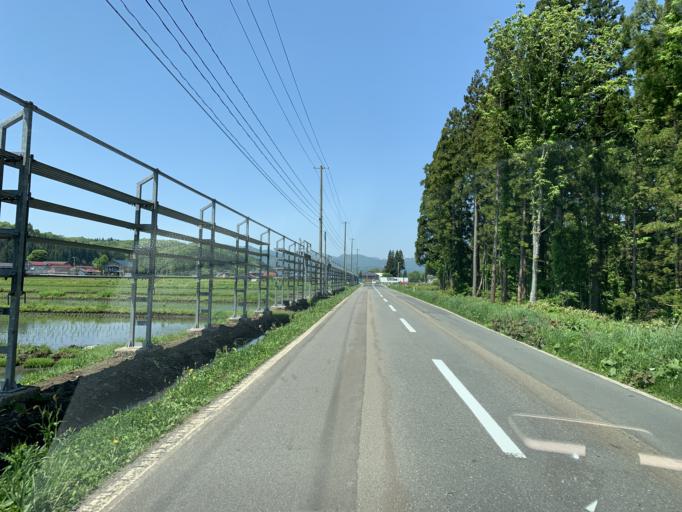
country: JP
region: Akita
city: Yokotemachi
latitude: 39.3781
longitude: 140.7599
